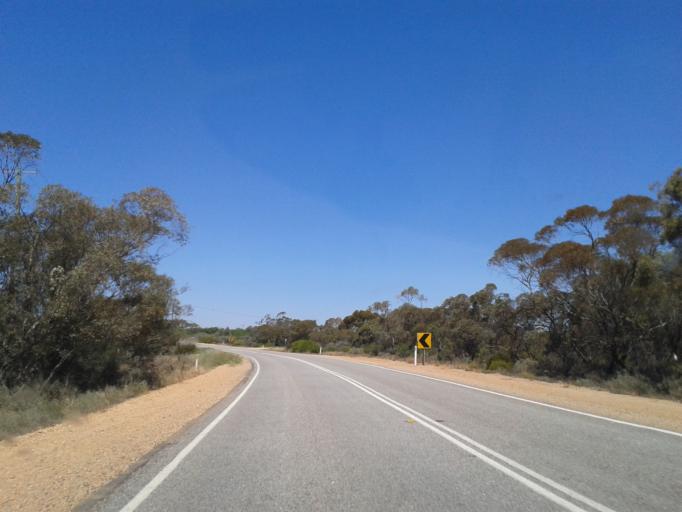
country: AU
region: Victoria
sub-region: Mildura Shire
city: Ouyen
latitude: -34.6777
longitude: 142.8433
